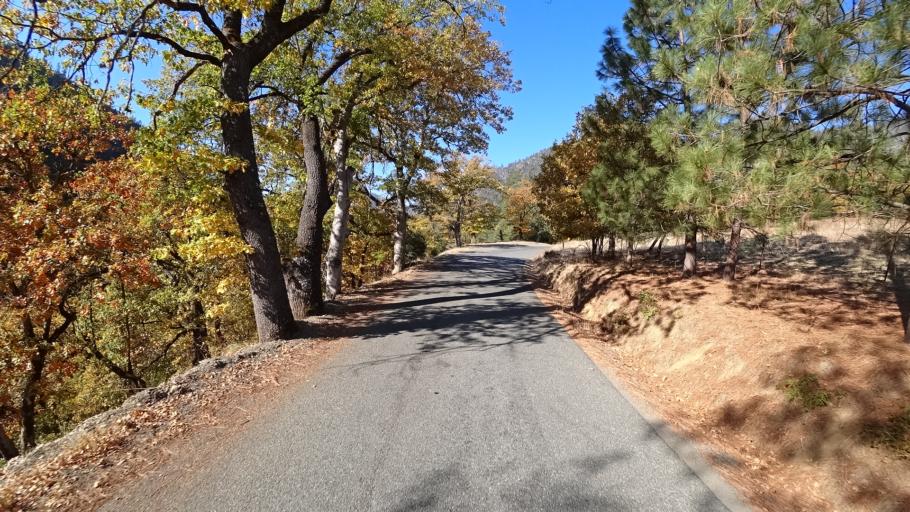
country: US
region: California
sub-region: Siskiyou County
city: Happy Camp
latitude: 41.6916
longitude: -123.0704
